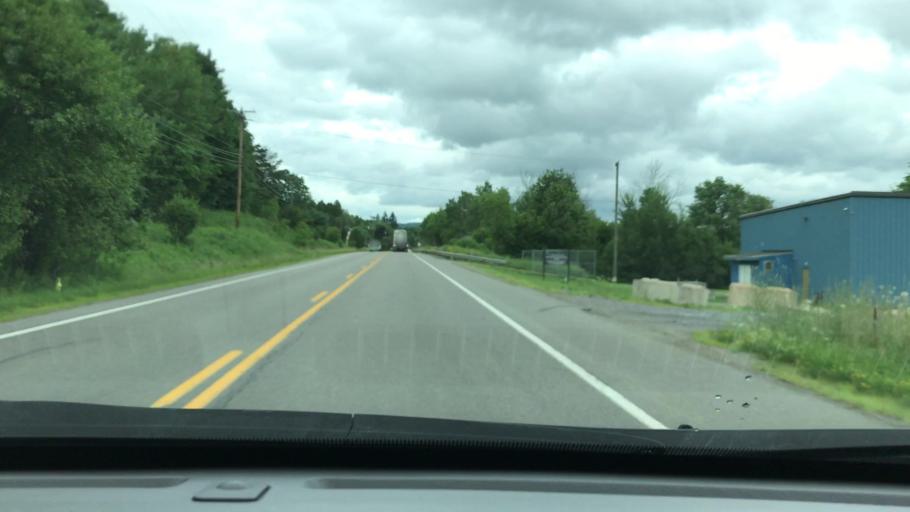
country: US
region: Pennsylvania
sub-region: Elk County
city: Ridgway
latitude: 41.3082
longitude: -78.6877
